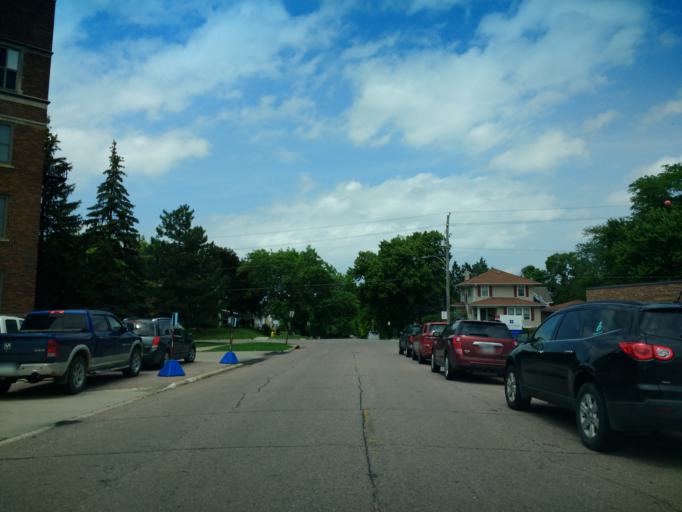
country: US
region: Iowa
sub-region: Woodbury County
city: Sioux City
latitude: 42.5202
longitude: -96.4067
